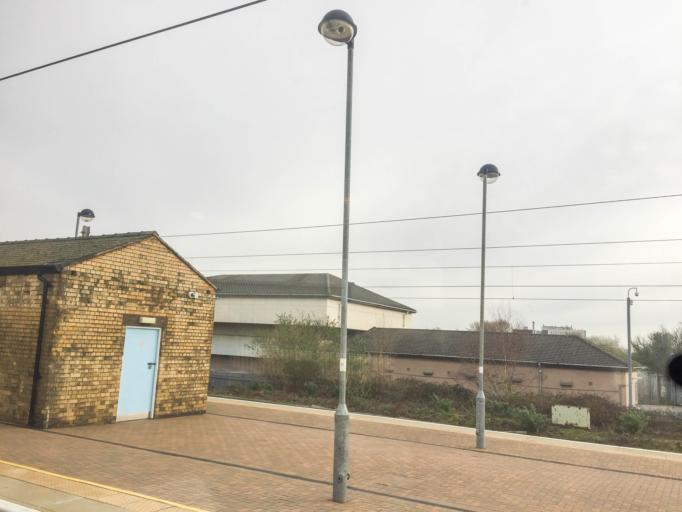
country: GB
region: England
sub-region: Warrington
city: Warrington
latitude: 53.3847
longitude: -2.6028
